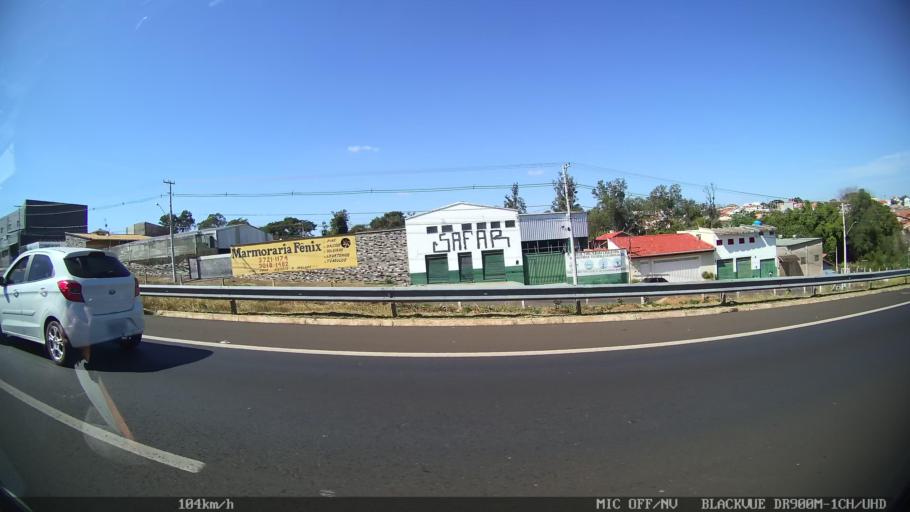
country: BR
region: Sao Paulo
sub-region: Franca
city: Franca
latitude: -20.5097
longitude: -47.4124
